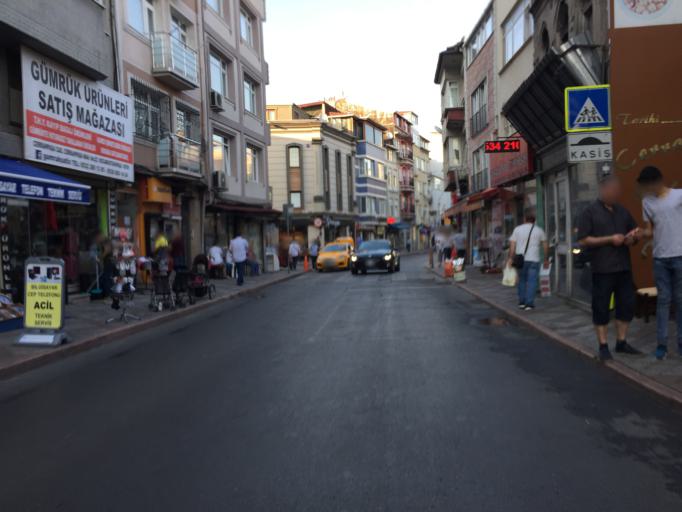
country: TR
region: Istanbul
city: Istanbul
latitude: 41.0073
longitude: 28.9429
